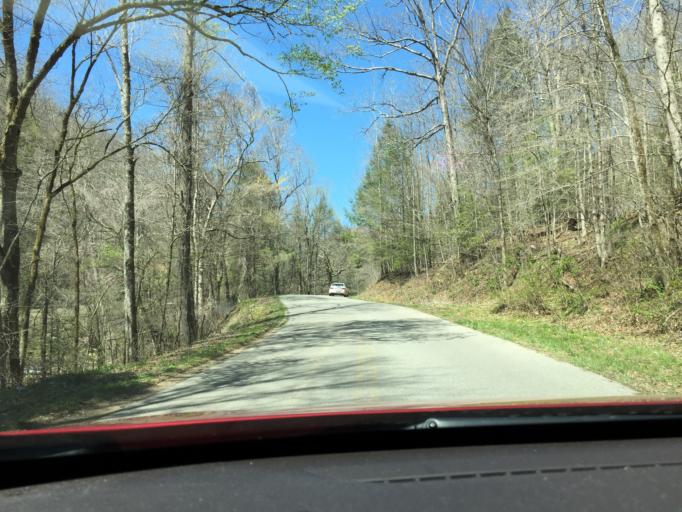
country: US
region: Tennessee
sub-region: Campbell County
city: Caryville
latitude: 36.3557
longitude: -84.2634
